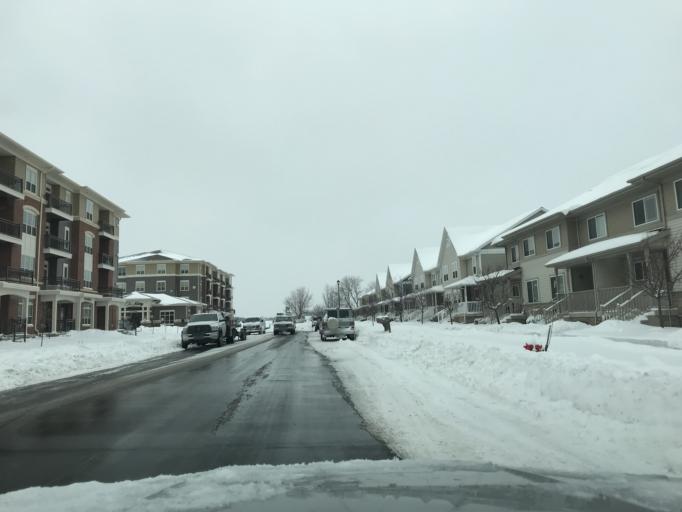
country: US
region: Wisconsin
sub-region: Dane County
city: Sun Prairie
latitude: 43.1717
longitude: -89.2729
